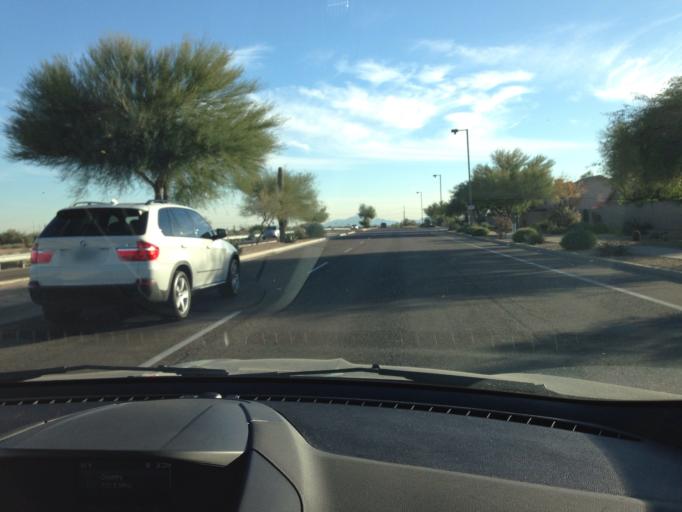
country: US
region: Arizona
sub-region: Maricopa County
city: Cave Creek
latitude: 33.7223
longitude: -111.9775
